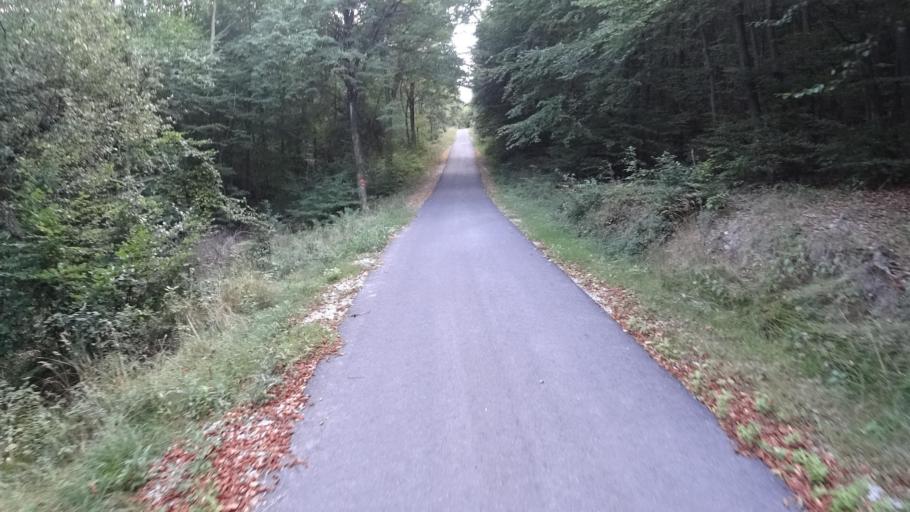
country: DE
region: Rheinland-Pfalz
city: Dichtelbach
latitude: 49.9855
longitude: 7.6922
